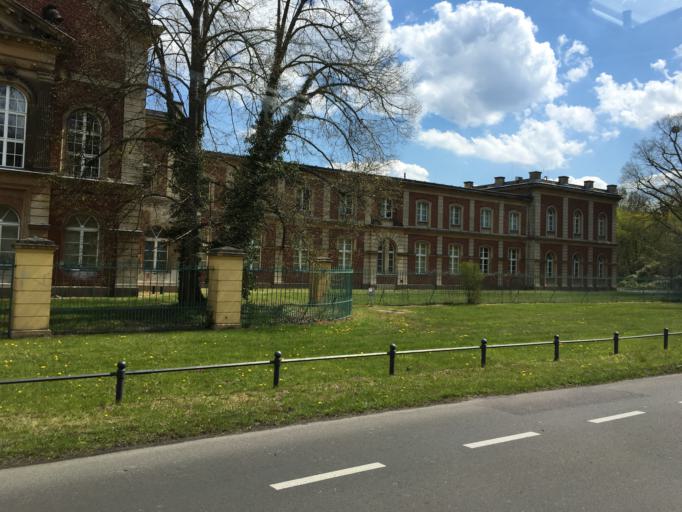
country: DE
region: Brandenburg
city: Potsdam
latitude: 52.3997
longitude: 13.0110
